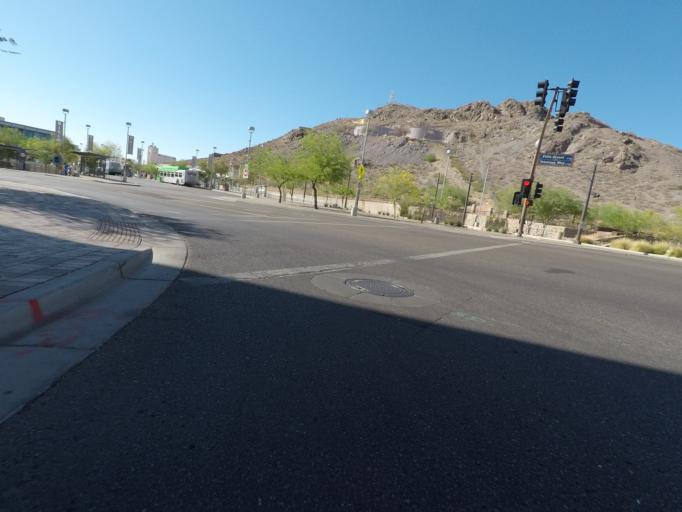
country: US
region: Arizona
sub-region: Maricopa County
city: Tempe Junction
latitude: 33.4254
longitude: -111.9351
